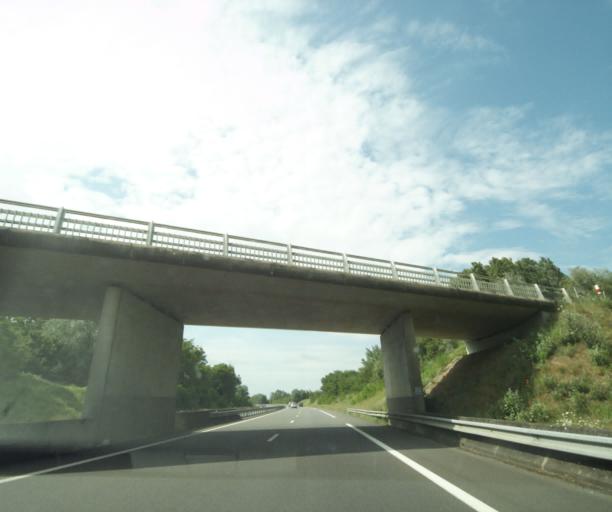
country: FR
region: Pays de la Loire
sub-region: Departement de Maine-et-Loire
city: Saint-Philbert-du-Peuple
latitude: 47.3801
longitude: -0.0866
